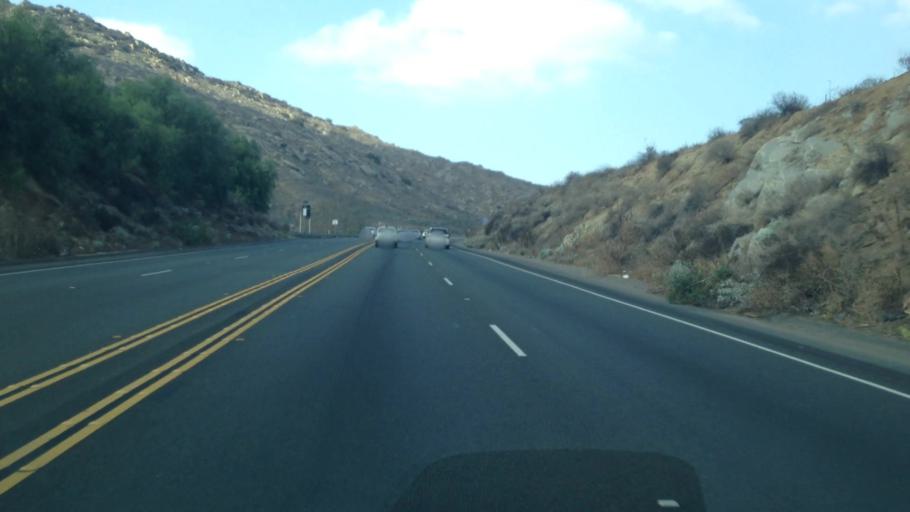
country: US
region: California
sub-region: Riverside County
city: Sunnyslope
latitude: 34.0330
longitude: -117.4321
